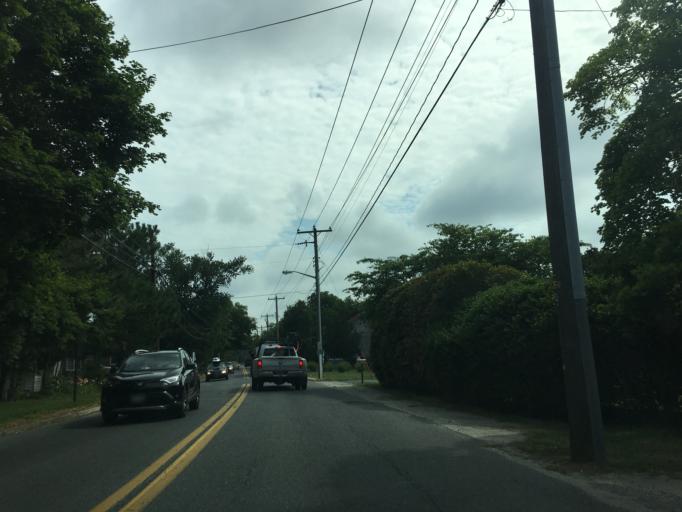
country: US
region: Delaware
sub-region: Sussex County
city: Ocean View
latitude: 38.5479
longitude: -75.0895
